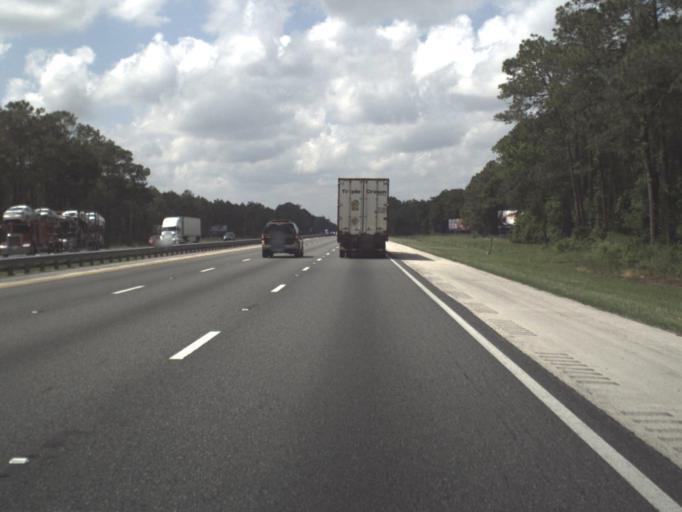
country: US
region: Florida
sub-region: Saint Johns County
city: Saint Augustine
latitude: 29.8905
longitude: -81.4037
